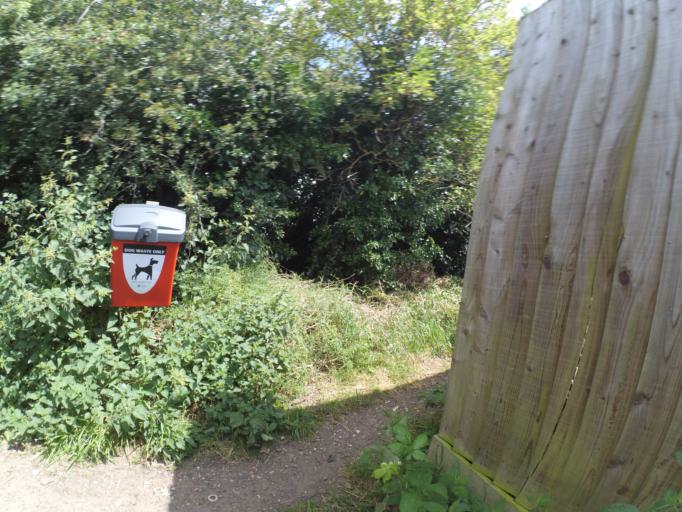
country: GB
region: England
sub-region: Warwickshire
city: Long Lawford
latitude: 52.3839
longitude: -1.3002
